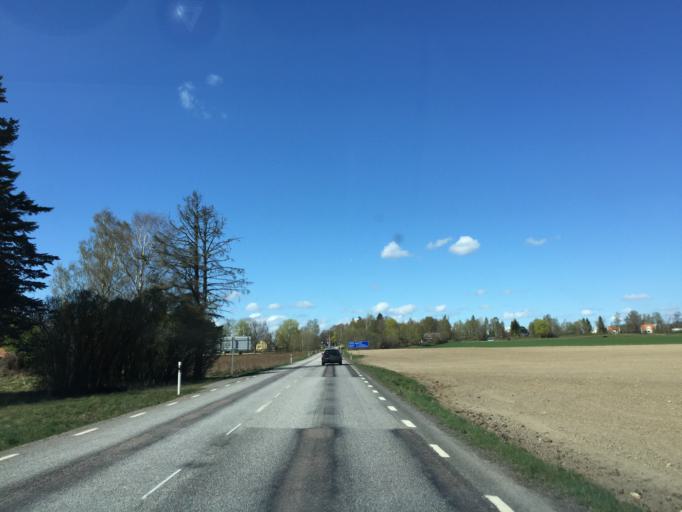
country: SE
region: OErebro
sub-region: Hallsbergs Kommun
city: Skollersta
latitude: 59.1256
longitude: 15.3273
